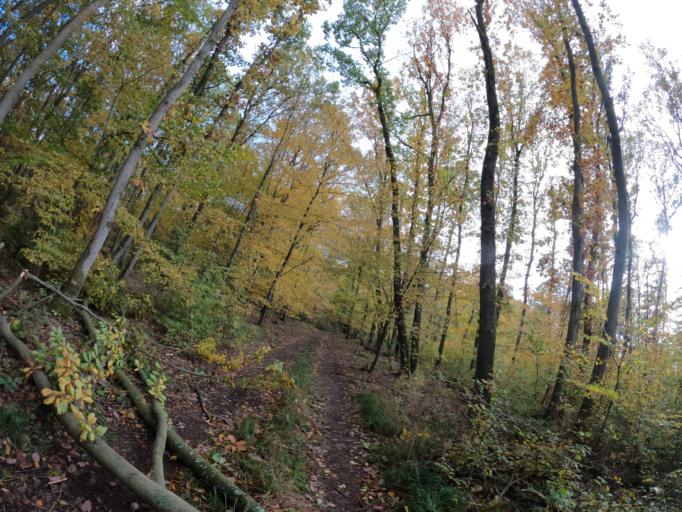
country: PL
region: West Pomeranian Voivodeship
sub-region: Powiat mysliborski
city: Barlinek
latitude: 52.9647
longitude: 15.2589
